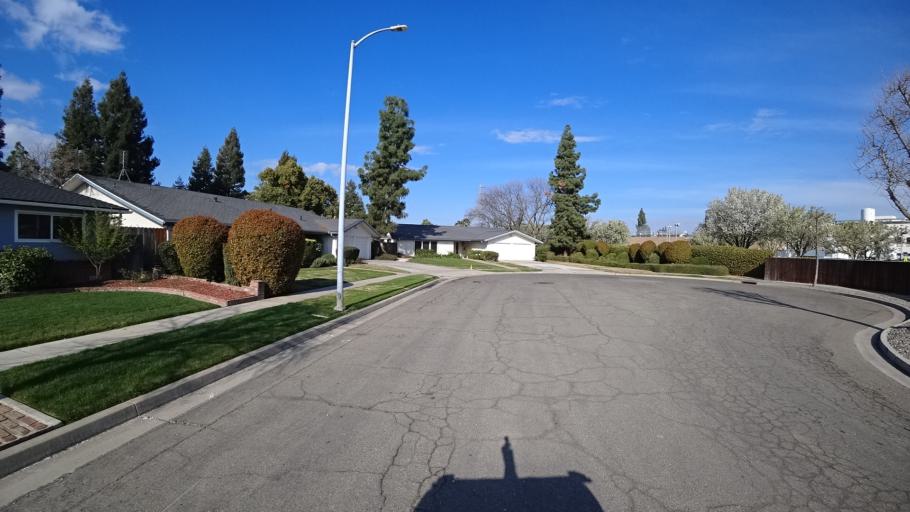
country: US
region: California
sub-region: Fresno County
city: Clovis
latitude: 36.8336
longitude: -119.7662
